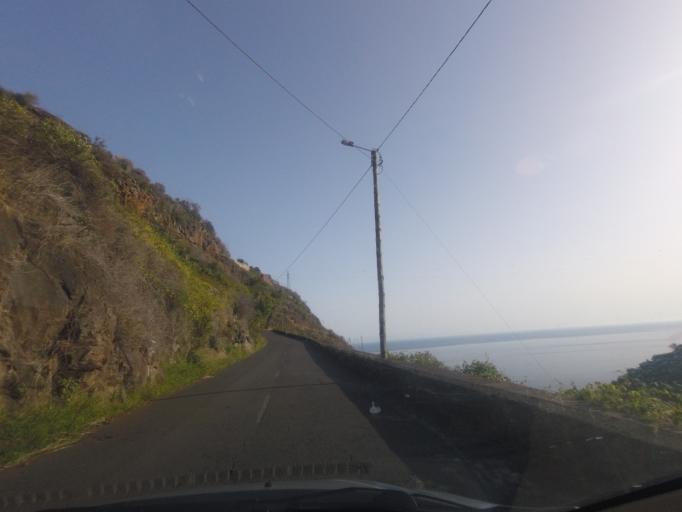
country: PT
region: Madeira
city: Ponta do Sol
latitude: 32.6858
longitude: -17.0824
